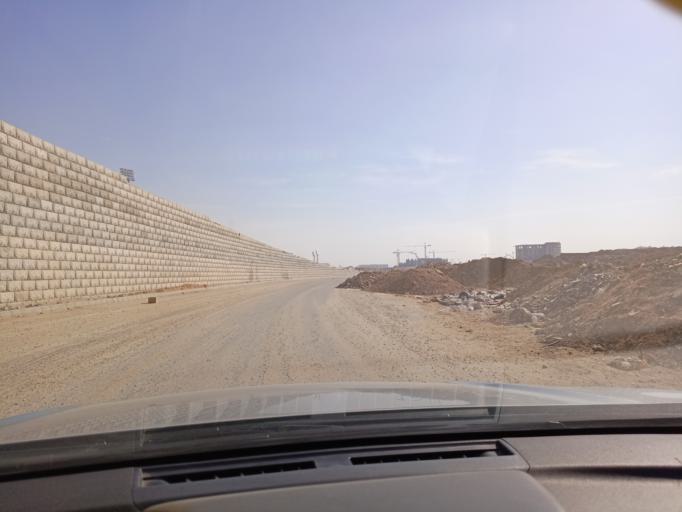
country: EG
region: Muhafazat al Qalyubiyah
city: Al Khankah
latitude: 30.0431
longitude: 31.6862
